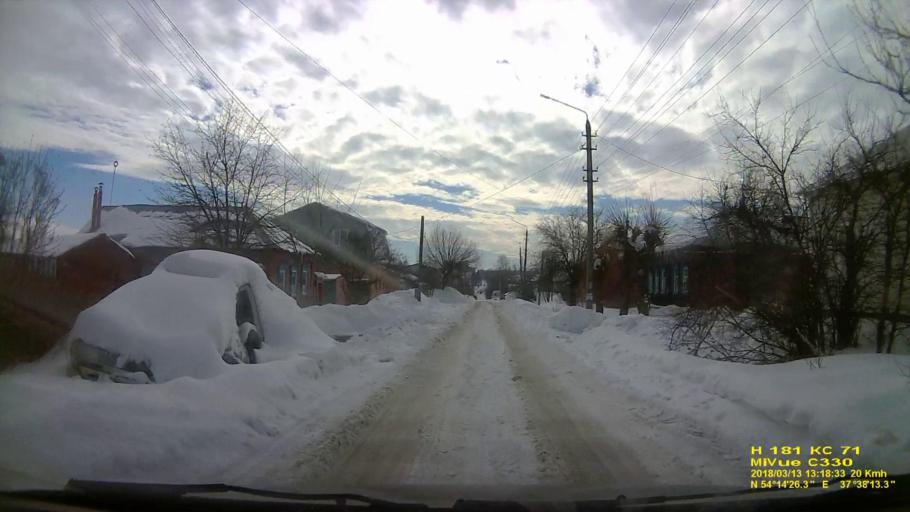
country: RU
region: Tula
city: Gorelki
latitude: 54.2406
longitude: 37.6370
